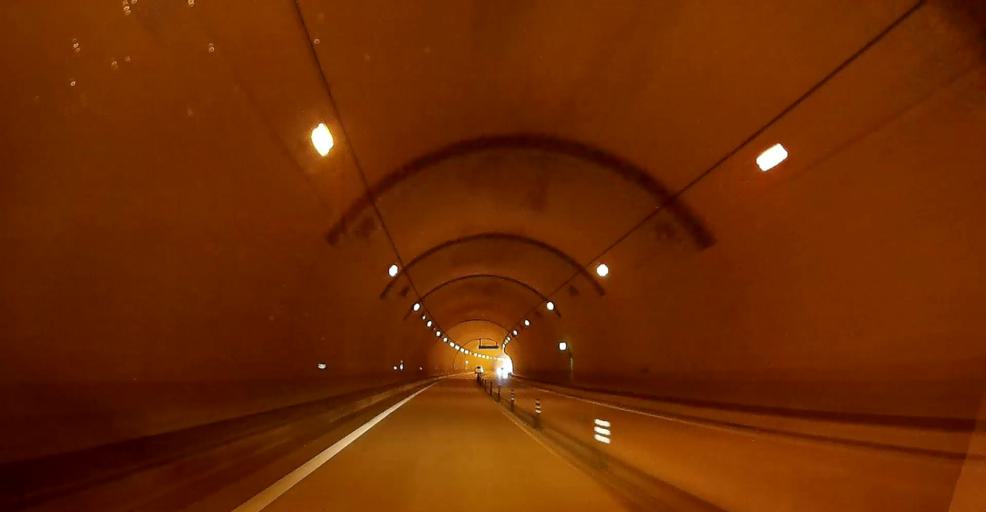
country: JP
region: Kumamoto
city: Yatsushiro
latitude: 32.5051
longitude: 130.4023
